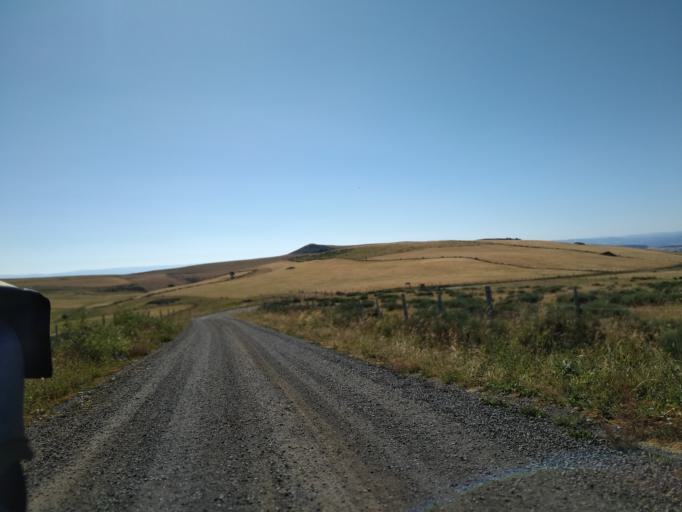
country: FR
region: Auvergne
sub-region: Departement du Cantal
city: Pierrefort
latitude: 45.0197
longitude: 2.8166
